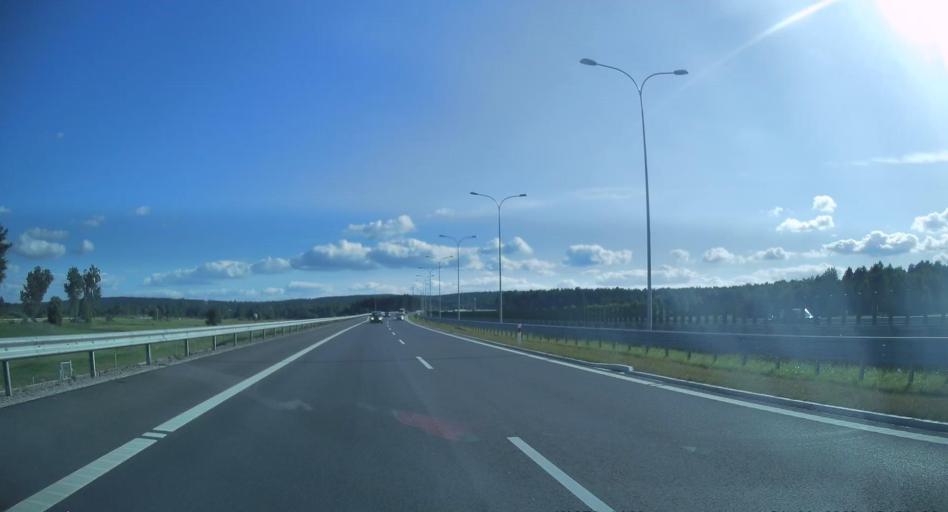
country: PL
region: Swietokrzyskie
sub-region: Powiat skarzyski
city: Skarzysko-Kamienna
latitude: 51.1650
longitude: 20.8577
